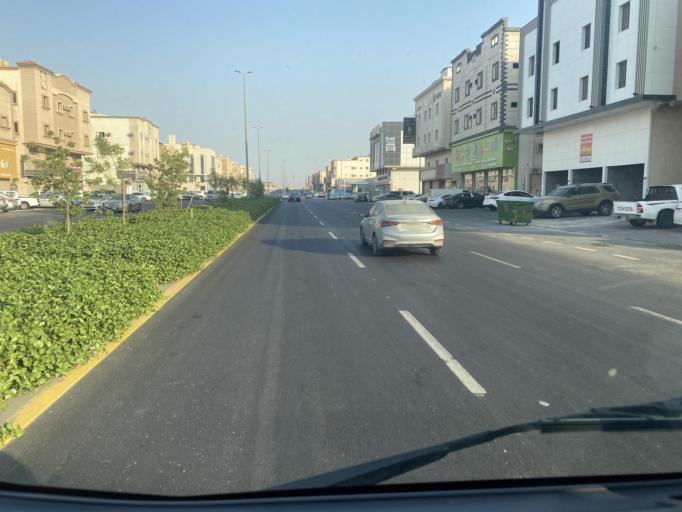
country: SA
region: Eastern Province
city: Dhahran
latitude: 26.3559
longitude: 50.0468
